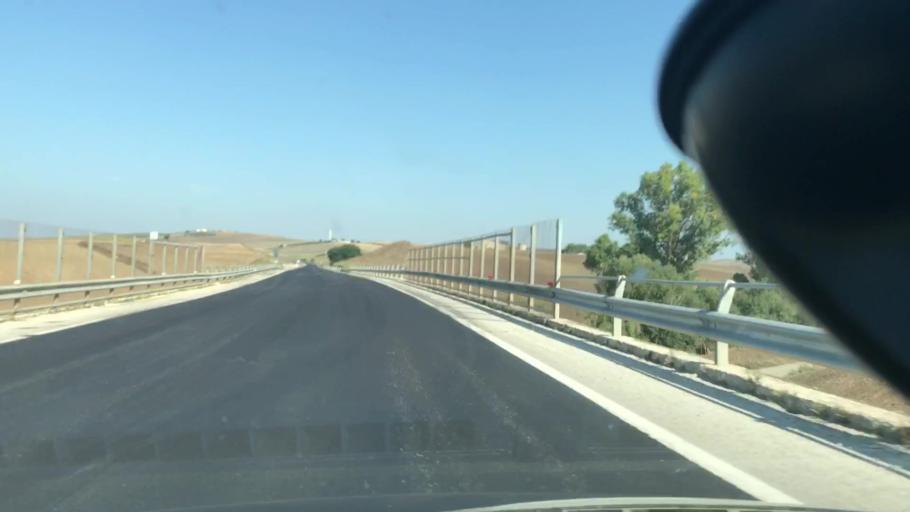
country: IT
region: Apulia
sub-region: Provincia di Barletta - Andria - Trani
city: Spinazzola
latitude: 40.9124
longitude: 16.1056
